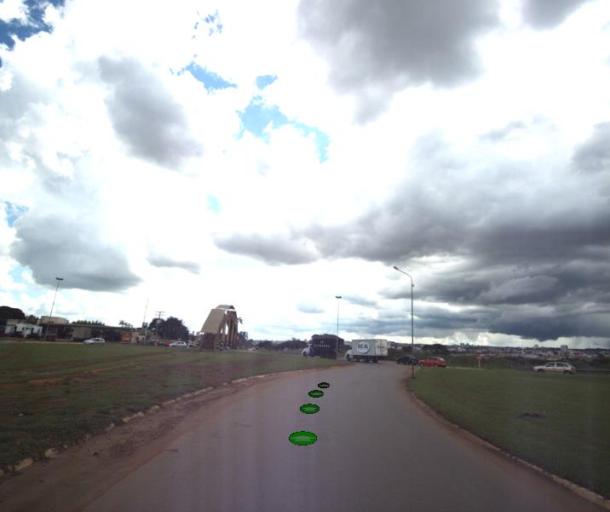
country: BR
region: Goias
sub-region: Anapolis
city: Anapolis
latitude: -16.3254
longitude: -48.9224
